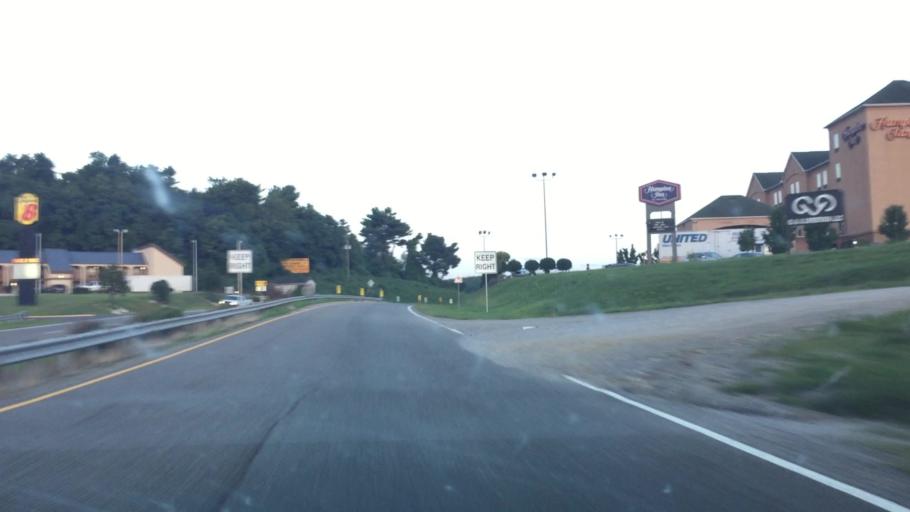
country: US
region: Virginia
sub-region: Wythe County
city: Wytheville
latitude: 36.9436
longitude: -80.9464
